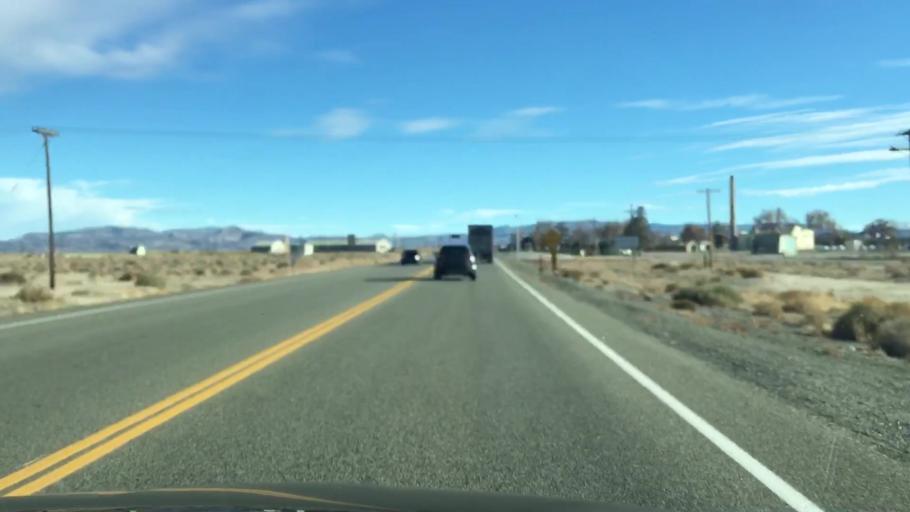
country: US
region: Nevada
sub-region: Mineral County
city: Hawthorne
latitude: 38.5505
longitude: -118.6563
